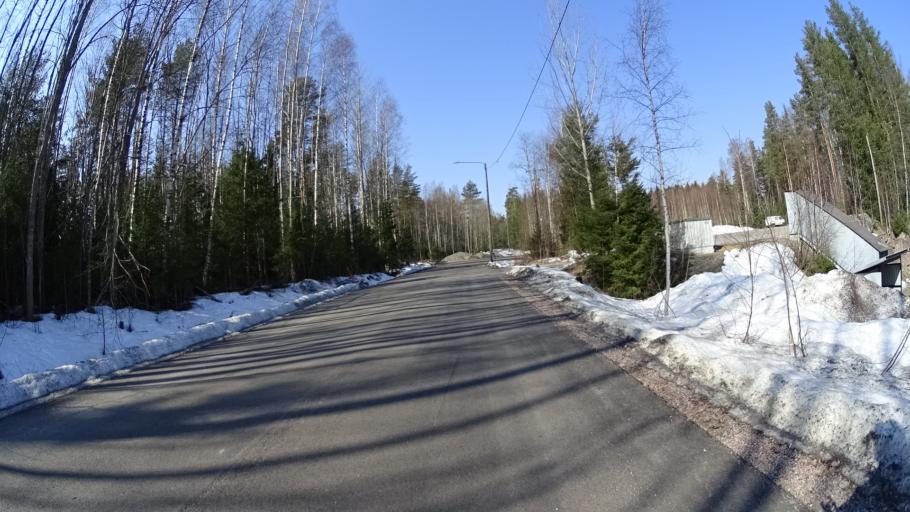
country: FI
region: Uusimaa
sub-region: Helsinki
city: Kirkkonummi
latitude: 60.2697
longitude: 24.4517
